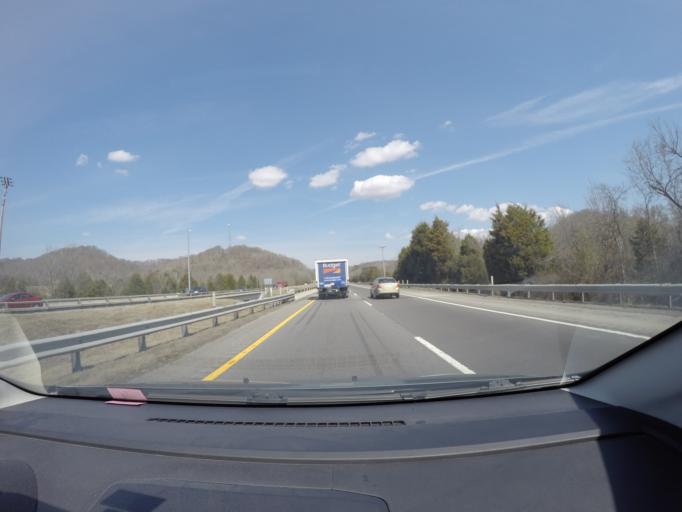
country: US
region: Tennessee
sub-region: Davidson County
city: Goodlettsville
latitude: 36.2928
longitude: -86.8103
